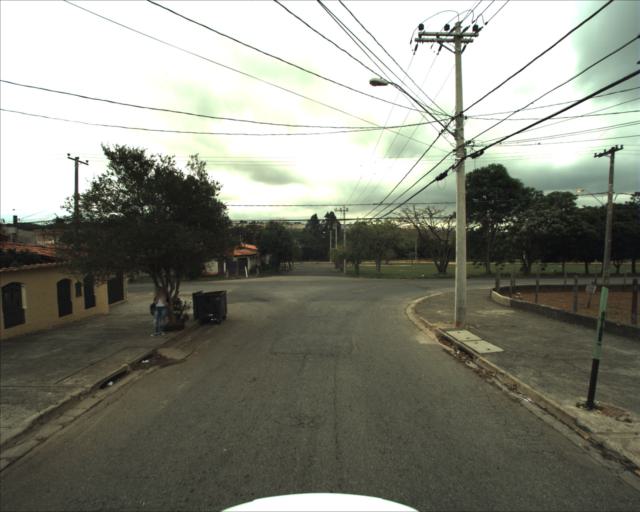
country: BR
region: Sao Paulo
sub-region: Sorocaba
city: Sorocaba
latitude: -23.4292
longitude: -47.5119
